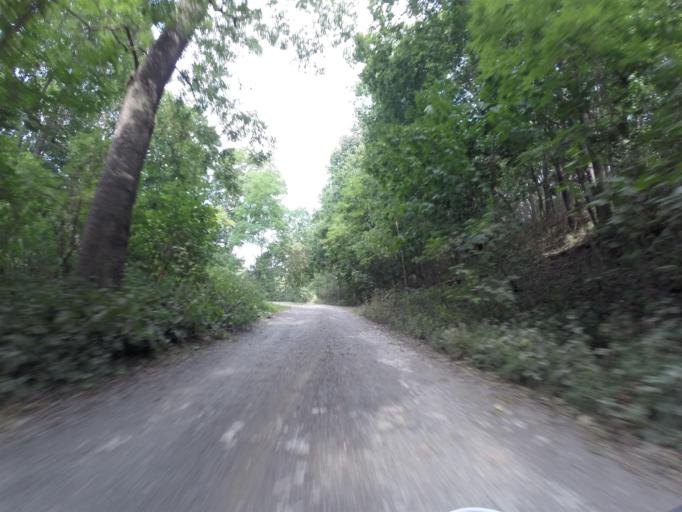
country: DE
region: Thuringia
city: Schloben
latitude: 50.8878
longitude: 11.6984
